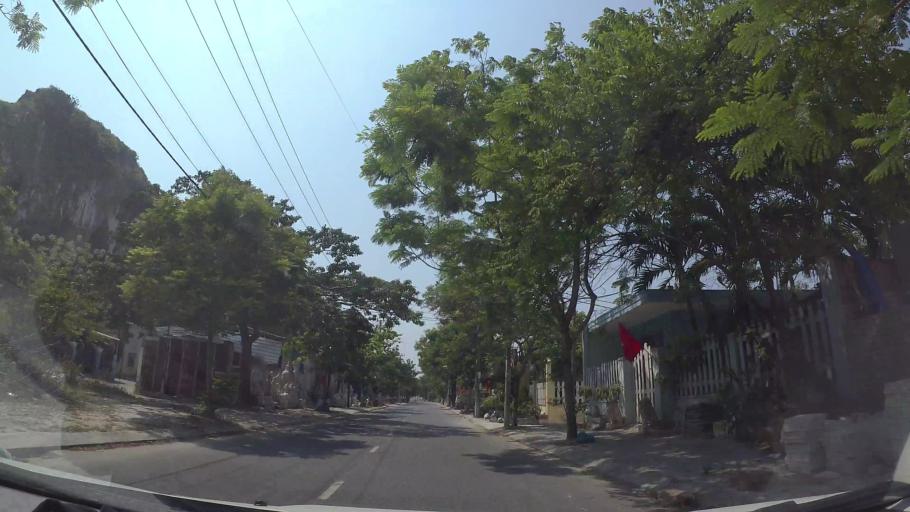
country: VN
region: Da Nang
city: Ngu Hanh Son
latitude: 16.0006
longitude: 108.2628
